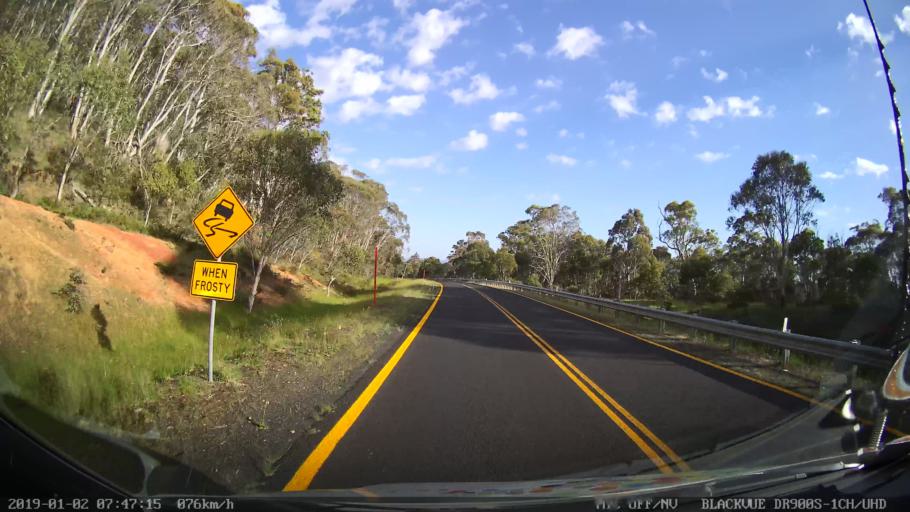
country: AU
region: New South Wales
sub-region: Tumut Shire
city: Tumut
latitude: -35.7667
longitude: 148.5216
